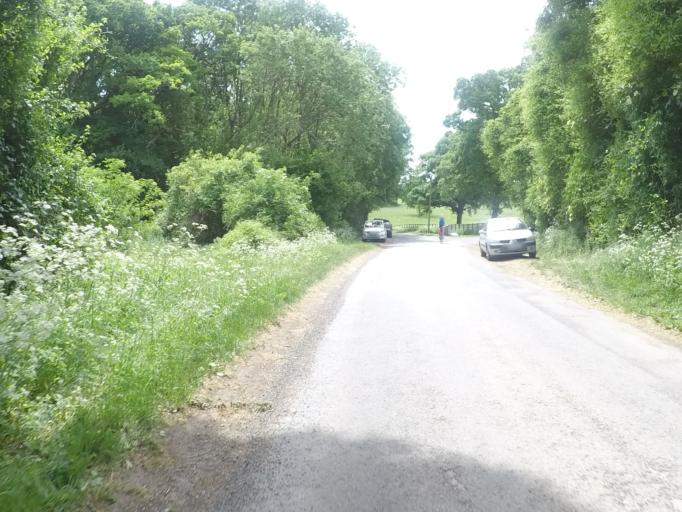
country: GB
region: England
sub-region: Oxfordshire
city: Charlbury
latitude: 51.8618
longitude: -1.5179
